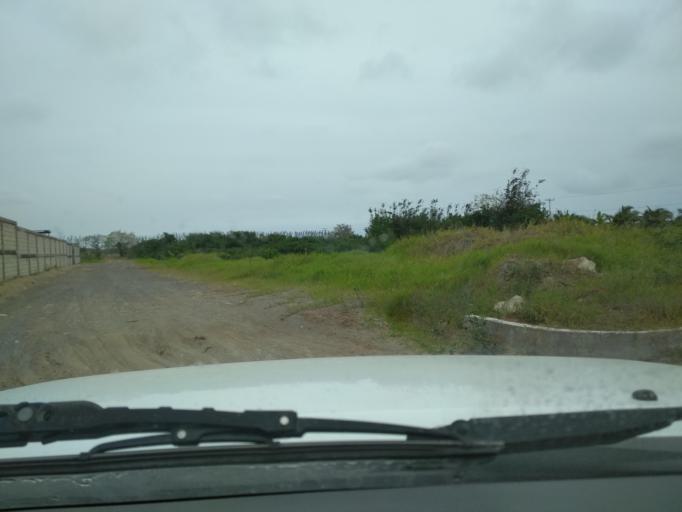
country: MX
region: Veracruz
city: Paso del Toro
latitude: 19.0426
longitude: -96.1329
